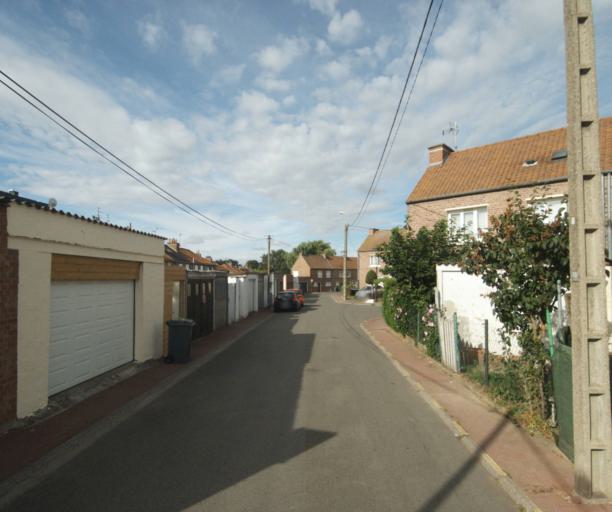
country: FR
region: Nord-Pas-de-Calais
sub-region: Departement du Nord
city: Linselles
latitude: 50.7404
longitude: 3.0763
